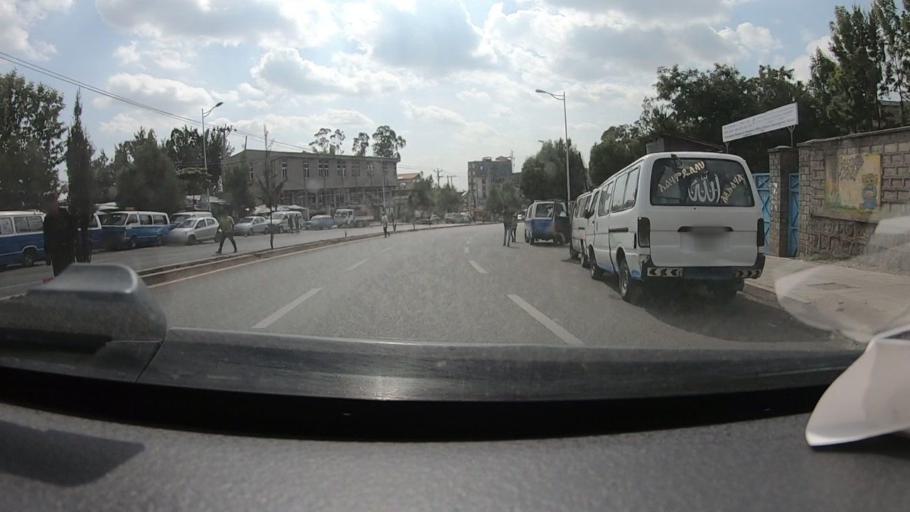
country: ET
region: Adis Abeba
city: Addis Ababa
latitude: 9.0580
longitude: 38.7786
